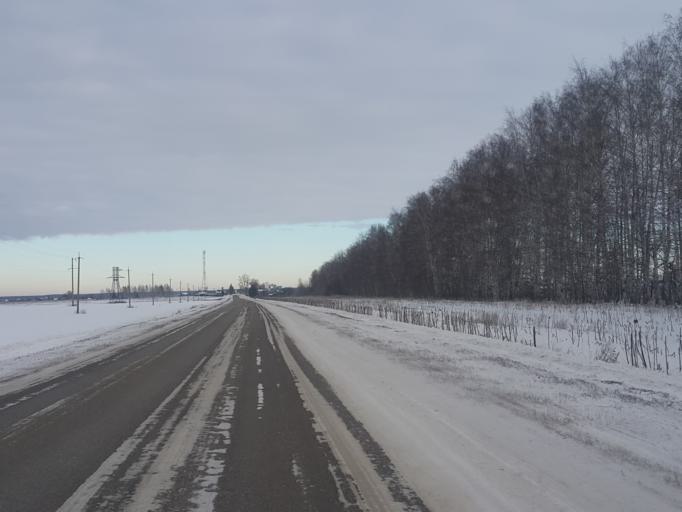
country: RU
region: Tambov
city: Rasskazovo
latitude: 52.8193
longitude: 41.7980
